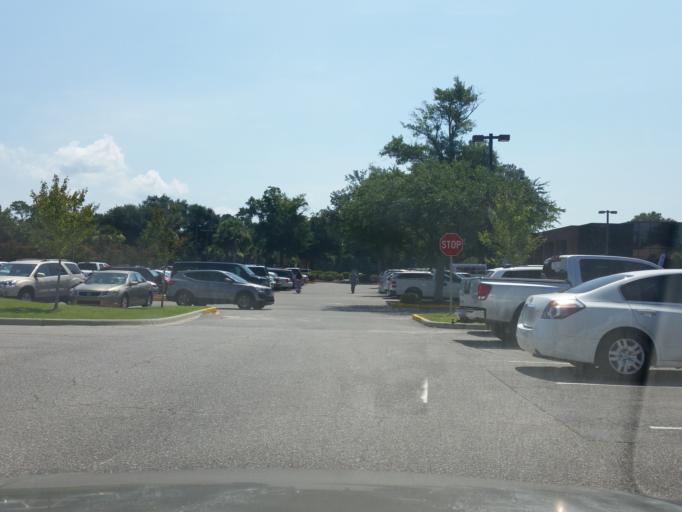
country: US
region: Florida
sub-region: Escambia County
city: Ferry Pass
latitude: 30.5128
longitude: -87.2231
